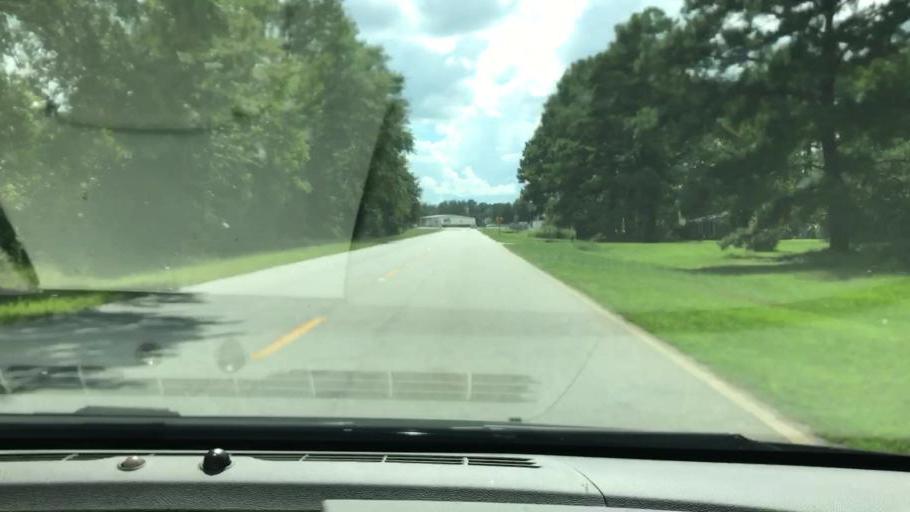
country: US
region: Georgia
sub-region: Quitman County
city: Georgetown
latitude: 31.8853
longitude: -85.0911
